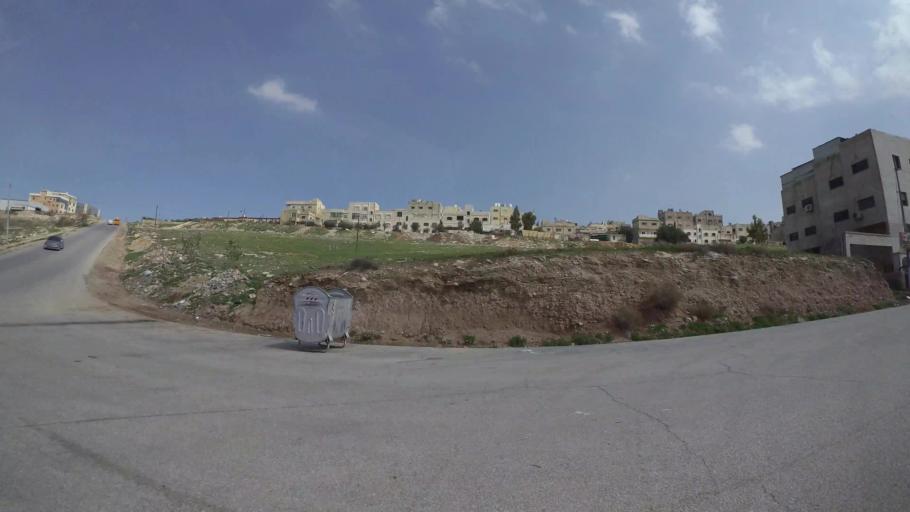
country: JO
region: Zarqa
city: Russeifa
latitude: 31.9950
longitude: 35.9952
